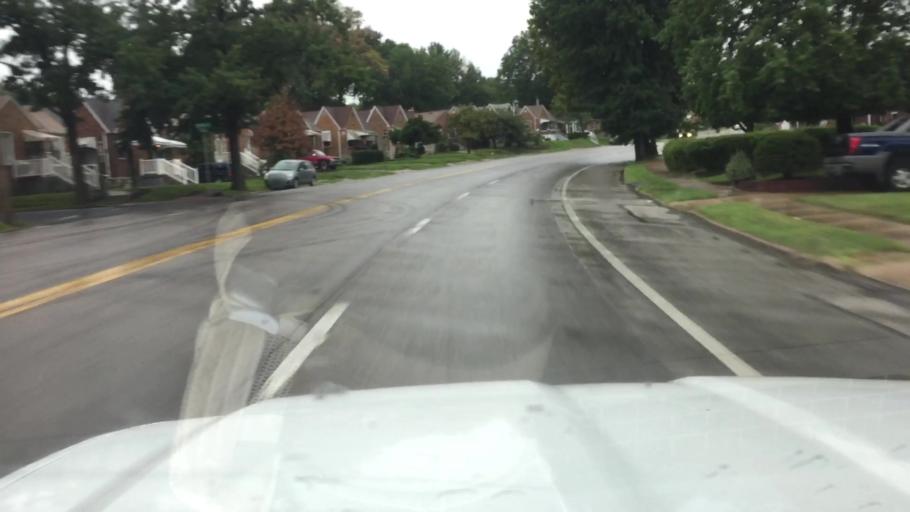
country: US
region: Missouri
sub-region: Saint Louis County
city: Lemay
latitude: 38.5141
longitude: -90.2859
